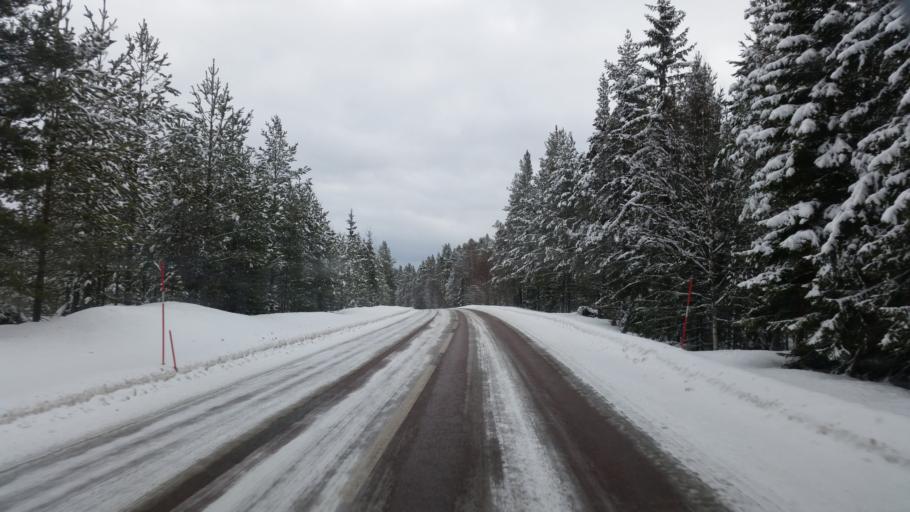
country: SE
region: Jaemtland
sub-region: Harjedalens Kommun
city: Sveg
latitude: 62.1819
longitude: 14.8782
